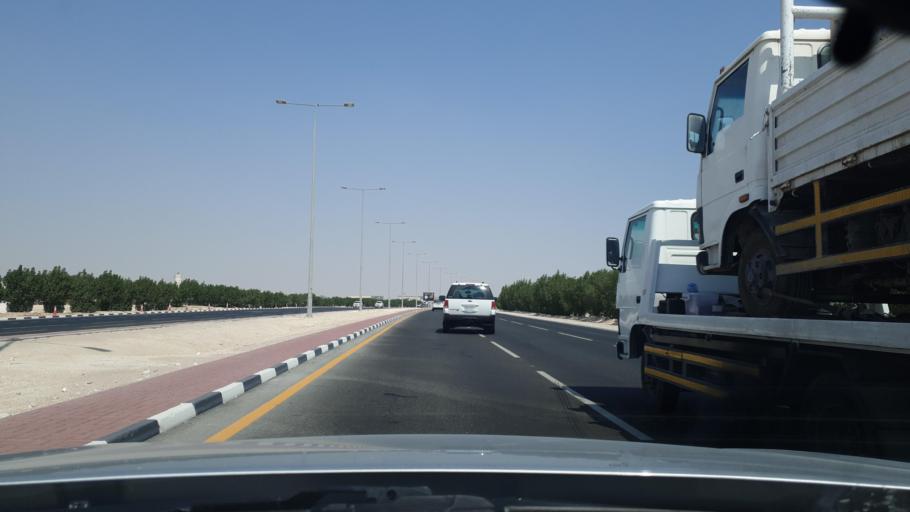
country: QA
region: Al Khawr
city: Al Khawr
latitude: 25.7075
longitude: 51.5051
